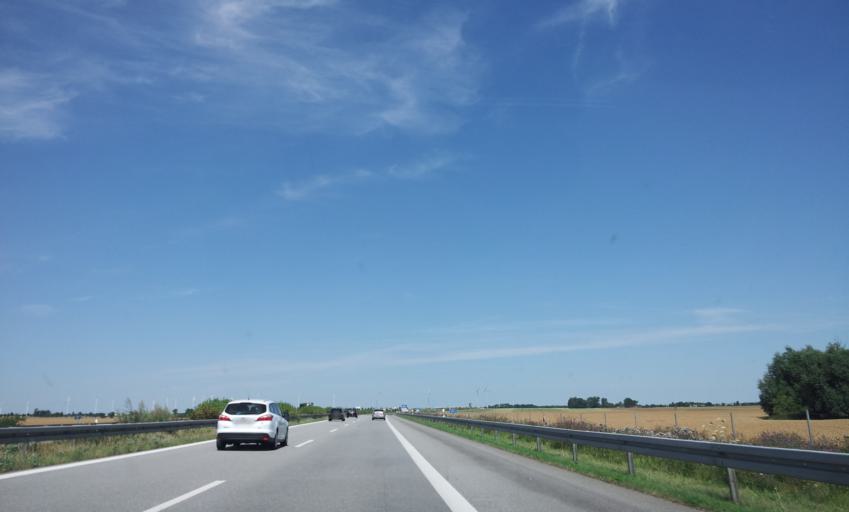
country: DE
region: Mecklenburg-Vorpommern
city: Jarmen
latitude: 53.8404
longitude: 13.3289
